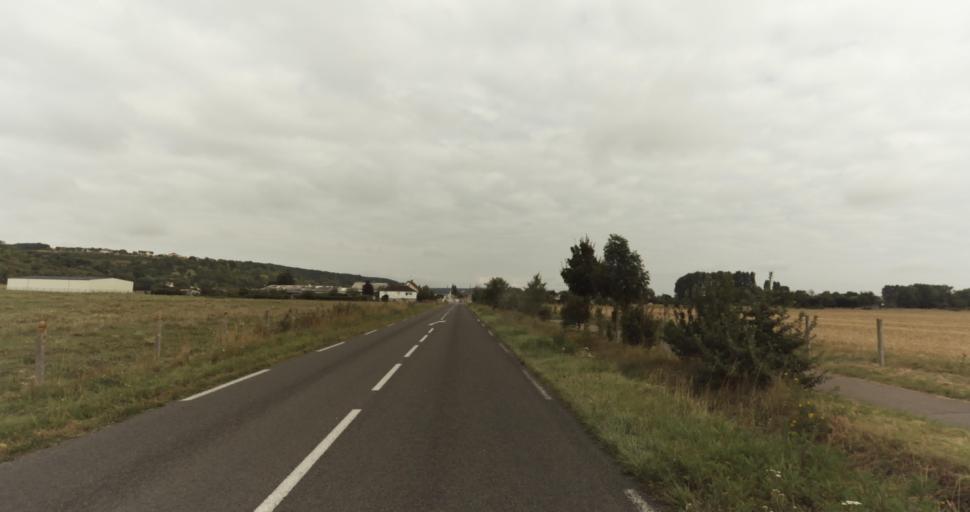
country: FR
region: Haute-Normandie
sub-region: Departement de l'Eure
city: Garennes-sur-Eure
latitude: 48.9058
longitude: 1.4447
